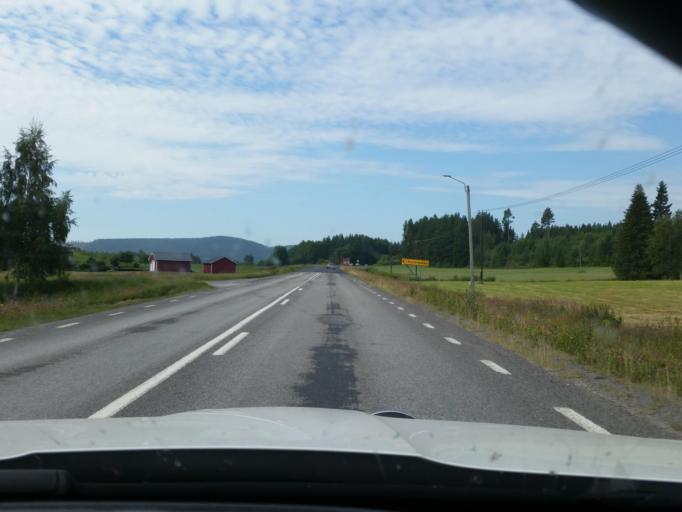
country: SE
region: Norrbotten
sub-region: Alvsbyns Kommun
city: AElvsbyn
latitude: 65.6802
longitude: 20.7821
